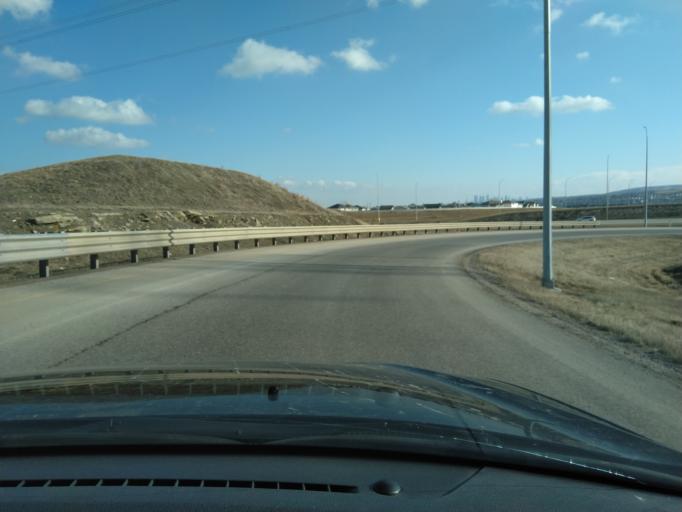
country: CA
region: Alberta
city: Calgary
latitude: 51.1746
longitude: -114.0671
